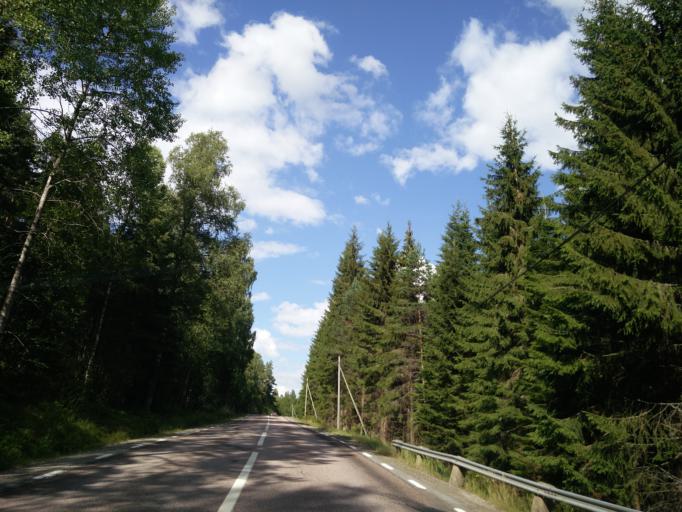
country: SE
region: Vaermland
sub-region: Sunne Kommun
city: Sunne
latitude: 59.6659
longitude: 12.9664
